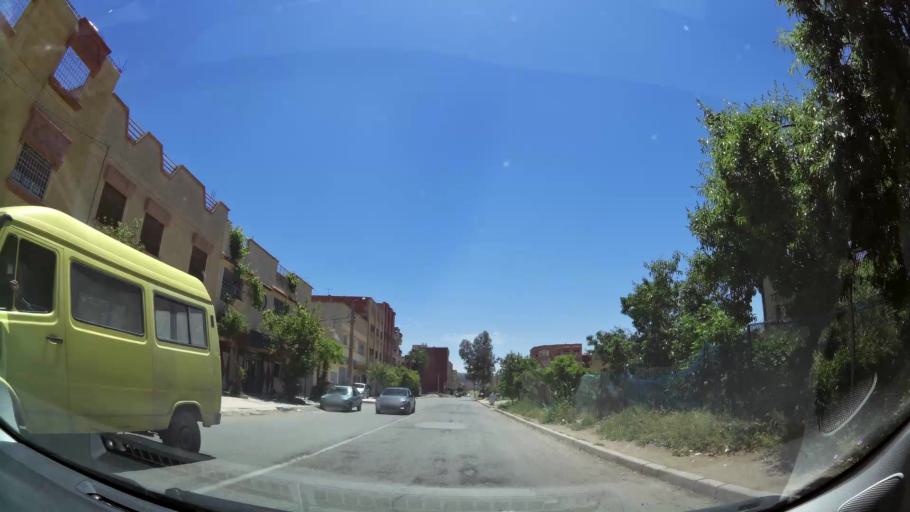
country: MA
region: Oriental
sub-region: Oujda-Angad
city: Oujda
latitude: 34.6772
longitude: -1.8754
